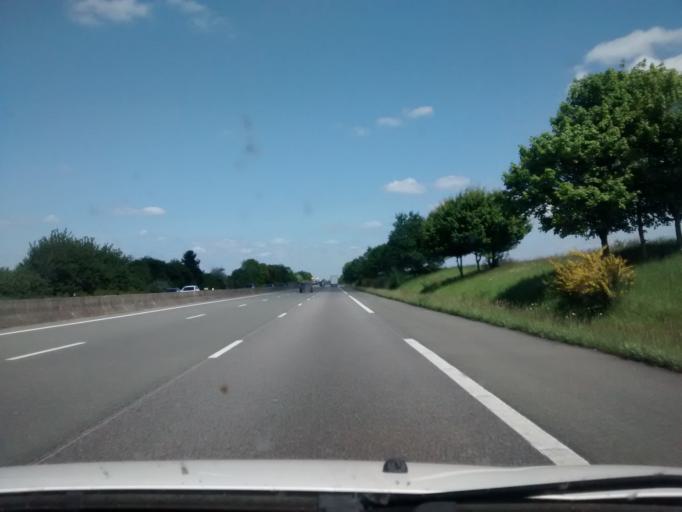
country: FR
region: Centre
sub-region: Departement d'Eure-et-Loir
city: Nogent-le-Phaye
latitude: 48.4738
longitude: 1.6084
